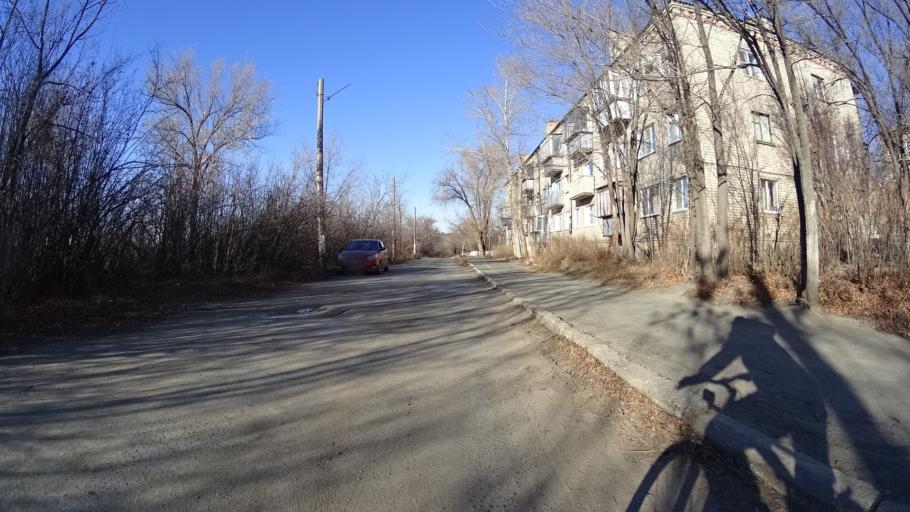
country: RU
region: Chelyabinsk
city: Troitsk
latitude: 54.0459
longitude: 61.6237
